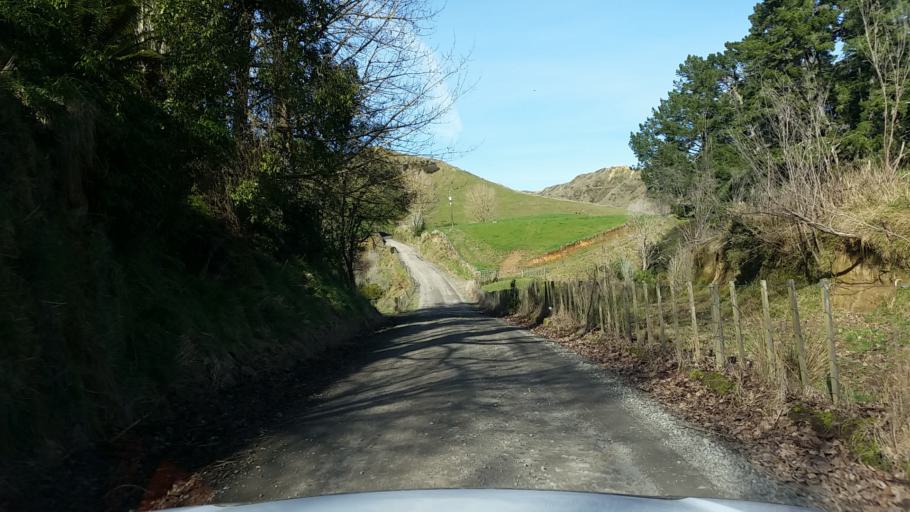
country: NZ
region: Taranaki
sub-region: South Taranaki District
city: Eltham
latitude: -39.3519
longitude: 174.5131
